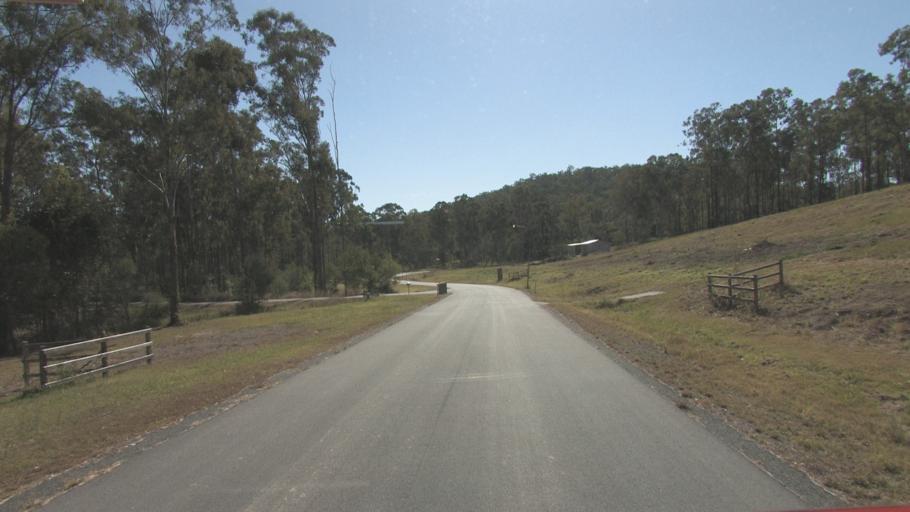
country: AU
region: Queensland
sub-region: Logan
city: Windaroo
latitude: -27.7737
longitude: 153.1458
